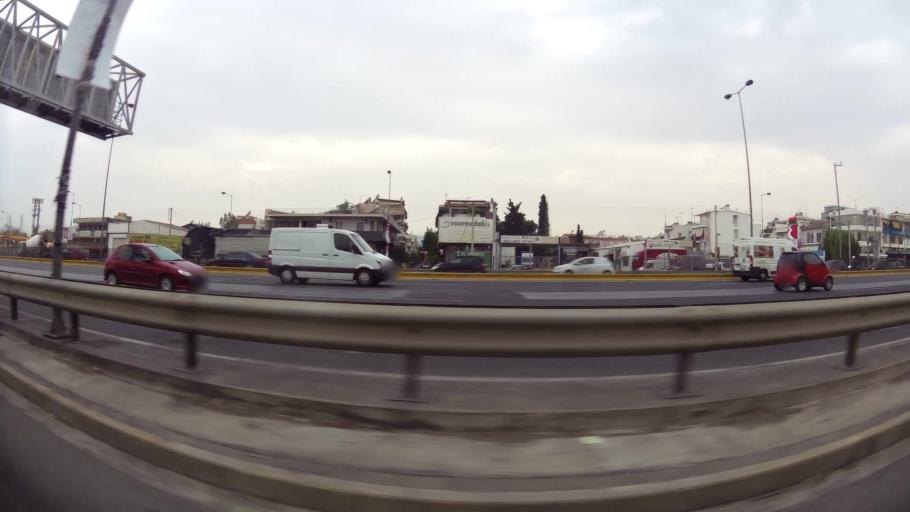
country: GR
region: Attica
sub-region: Nomarchia Athinas
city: Aigaleo
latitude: 37.9845
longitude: 23.6832
